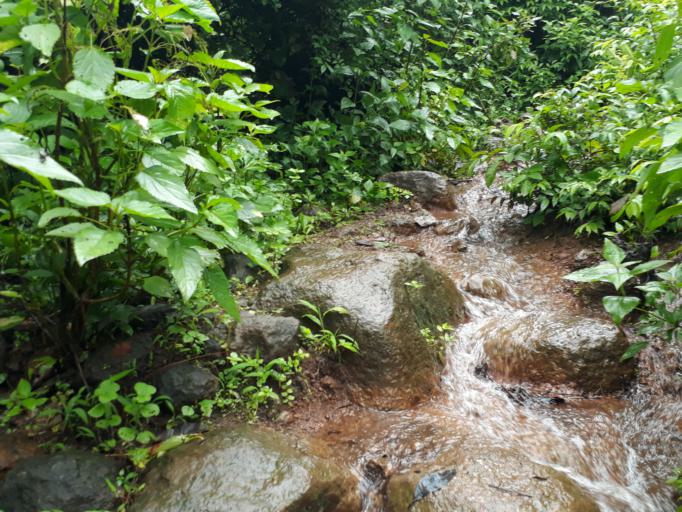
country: IN
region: Maharashtra
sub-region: Raigarh
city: Khopoli
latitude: 18.8441
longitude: 73.3790
